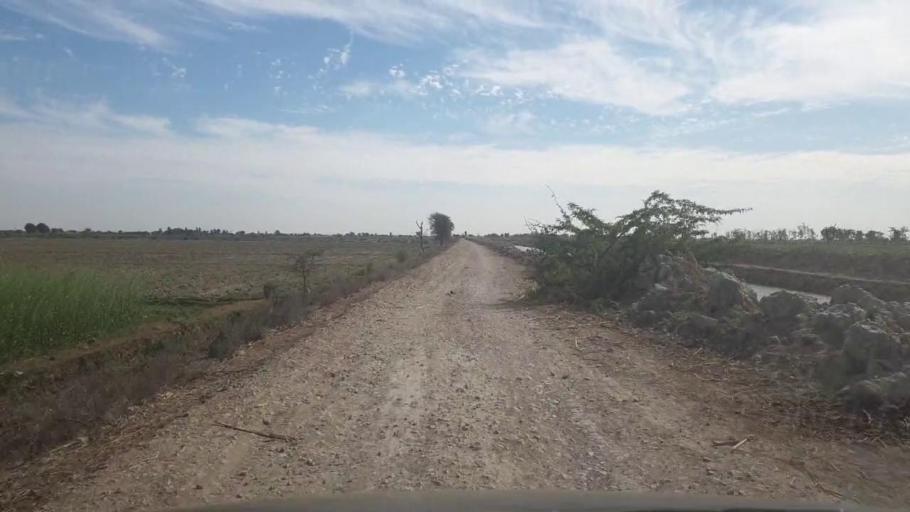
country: PK
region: Sindh
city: Mirwah Gorchani
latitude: 25.4283
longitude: 69.2003
